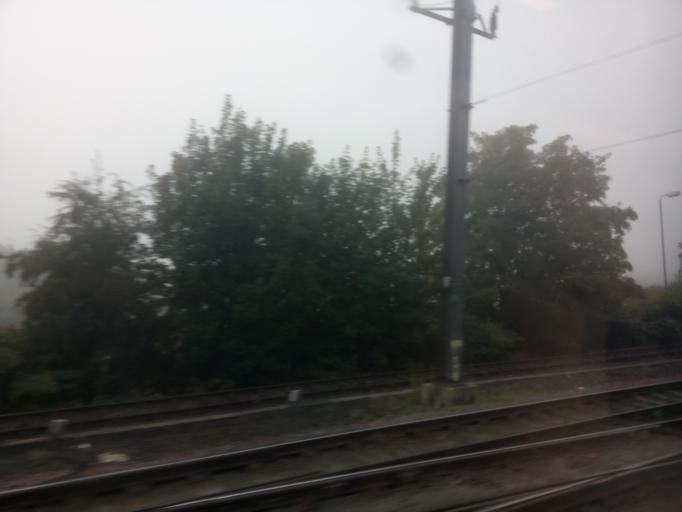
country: GB
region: England
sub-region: City and Borough of Leeds
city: Leeds
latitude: 53.7910
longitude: -1.5093
